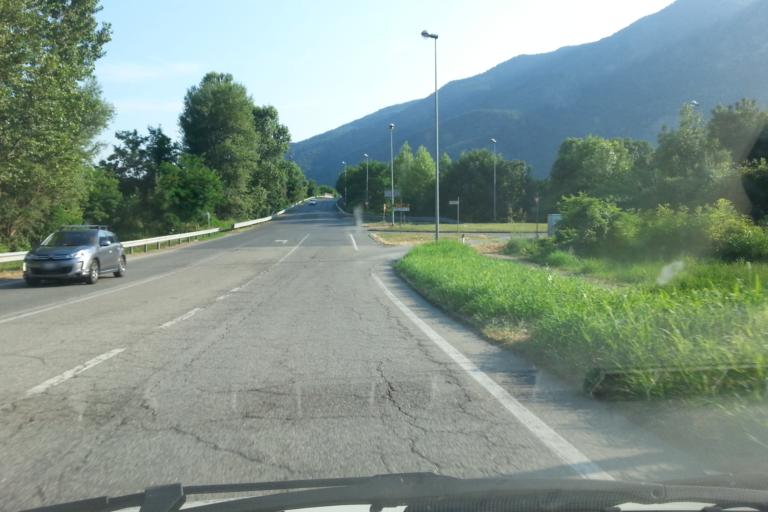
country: IT
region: Piedmont
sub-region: Provincia di Torino
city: Sant'Ambrogio di Torino
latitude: 45.0991
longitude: 7.3727
